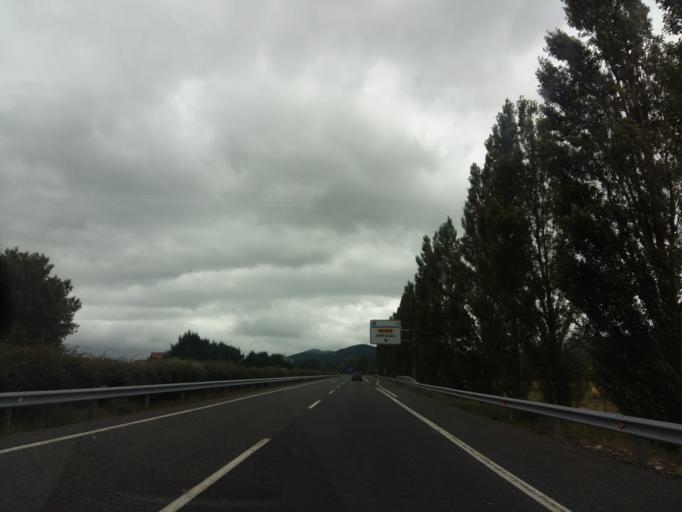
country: ES
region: Navarre
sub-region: Provincia de Navarra
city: Arruazu
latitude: 42.9228
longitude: -1.9944
